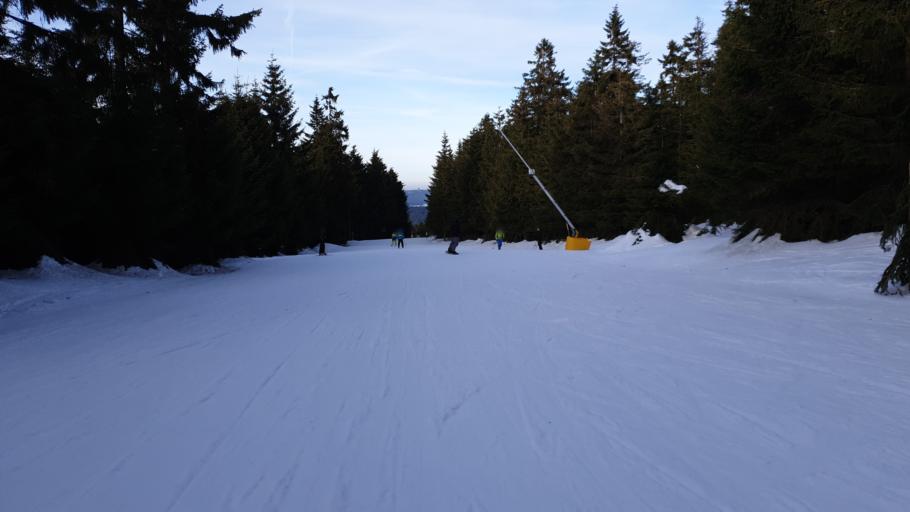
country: DE
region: Bavaria
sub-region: Upper Franconia
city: Bischofsgrun
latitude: 50.0350
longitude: 11.8108
